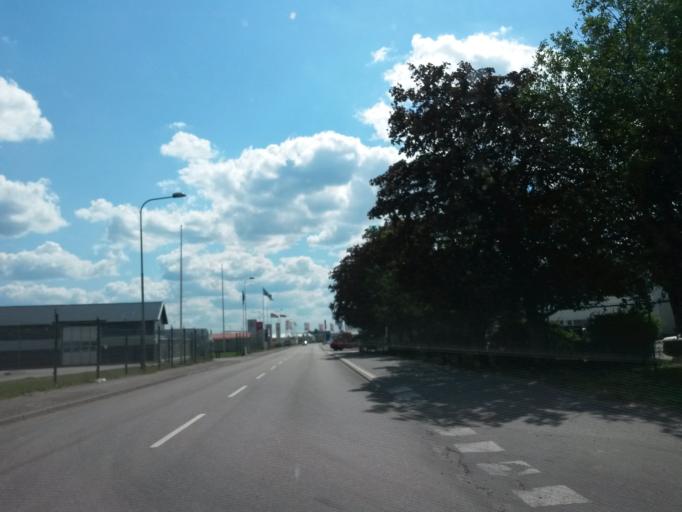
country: SE
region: Vaestra Goetaland
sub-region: Goteborg
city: Hammarkullen
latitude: 57.7758
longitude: 11.9940
